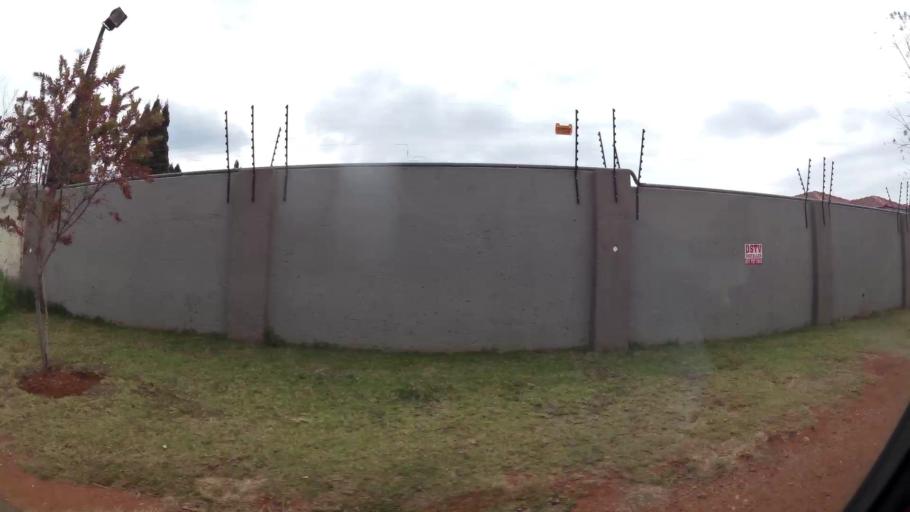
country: ZA
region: Gauteng
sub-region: West Rand District Municipality
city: Muldersdriseloop
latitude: -26.0902
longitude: 27.8758
